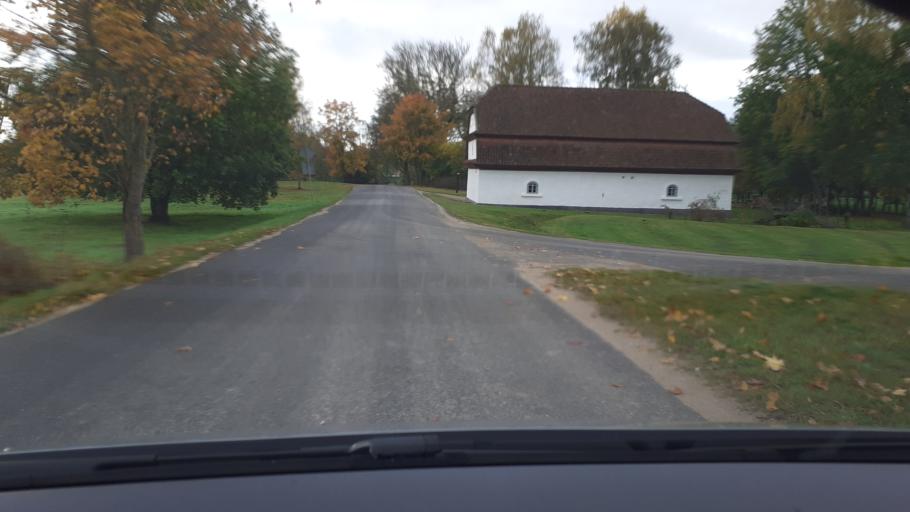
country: LV
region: Kuldigas Rajons
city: Kuldiga
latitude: 57.0204
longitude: 21.9135
